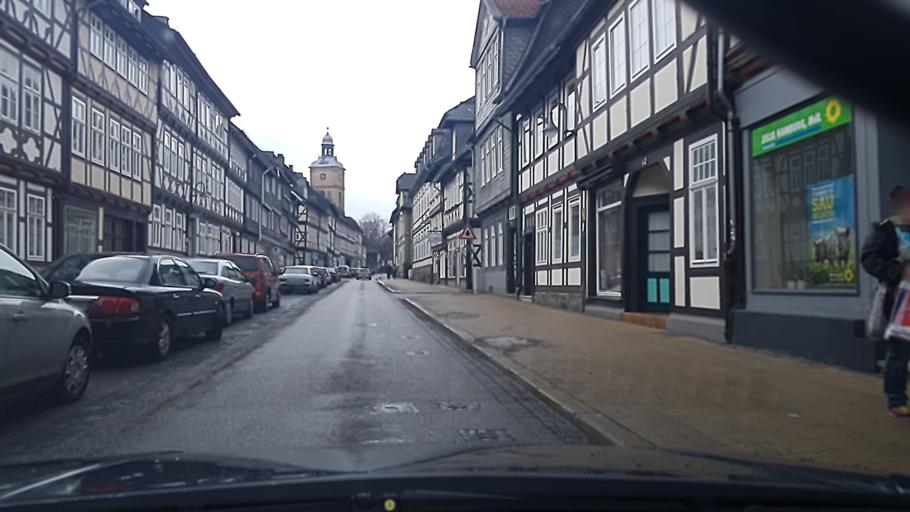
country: DE
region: Lower Saxony
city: Goslar
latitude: 51.9093
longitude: 10.4364
